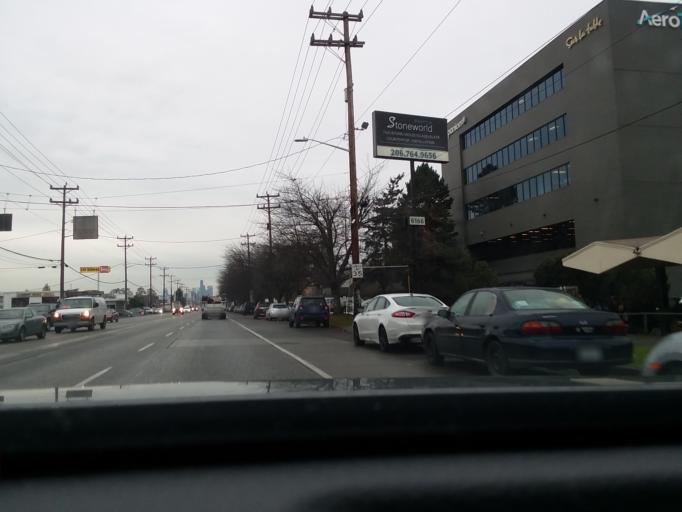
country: US
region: Washington
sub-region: King County
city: White Center
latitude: 47.5461
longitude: -122.3296
